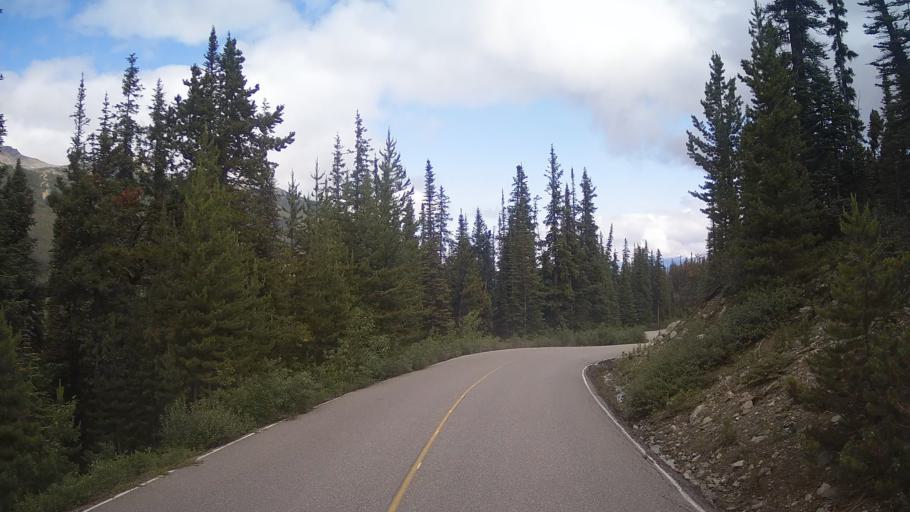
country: CA
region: Alberta
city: Jasper Park Lodge
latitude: 52.7107
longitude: -118.0561
